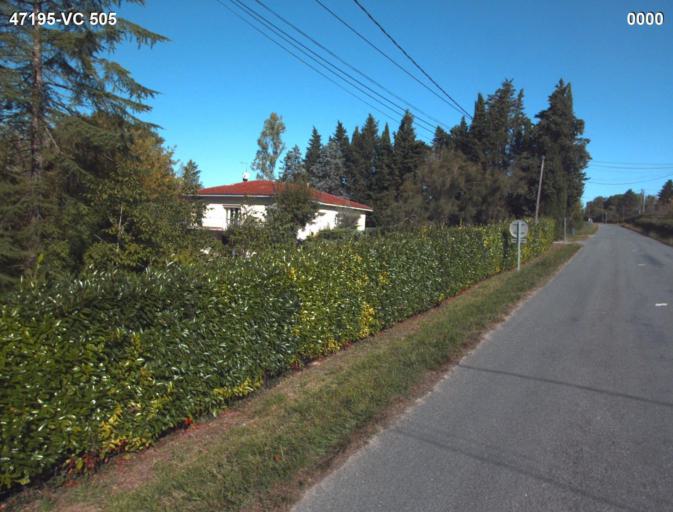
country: FR
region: Aquitaine
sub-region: Departement du Lot-et-Garonne
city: Nerac
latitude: 44.1410
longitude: 0.3616
